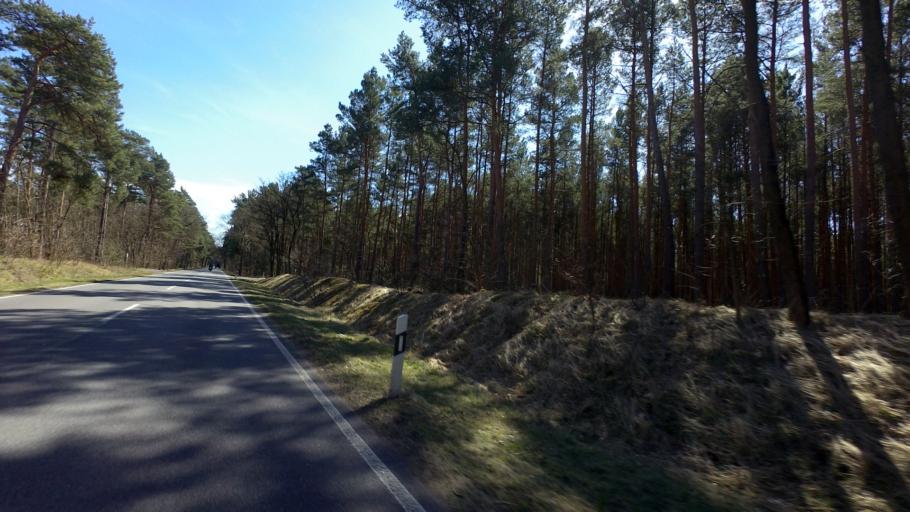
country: DE
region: Brandenburg
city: Teupitz
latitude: 52.1161
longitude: 13.6559
